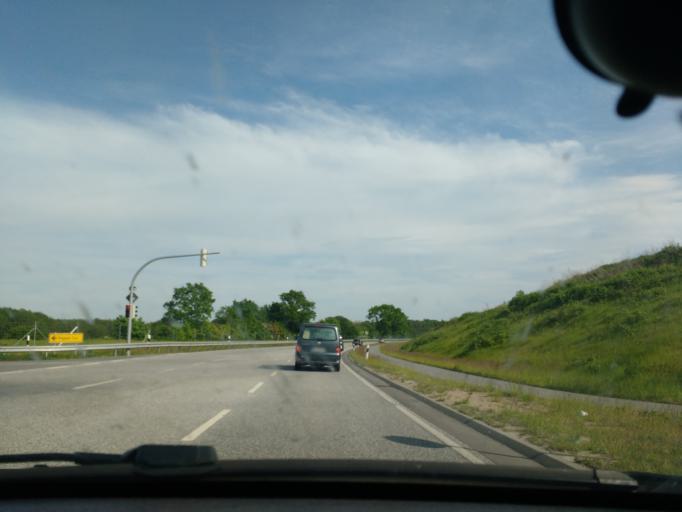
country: DE
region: Schleswig-Holstein
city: Pogeez
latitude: 53.7428
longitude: 10.7291
